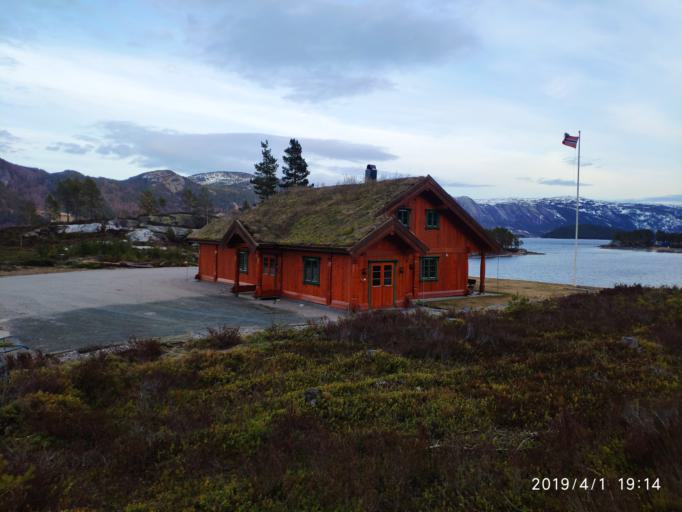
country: NO
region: Telemark
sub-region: Nissedal
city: Treungen
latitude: 59.1247
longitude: 8.4764
